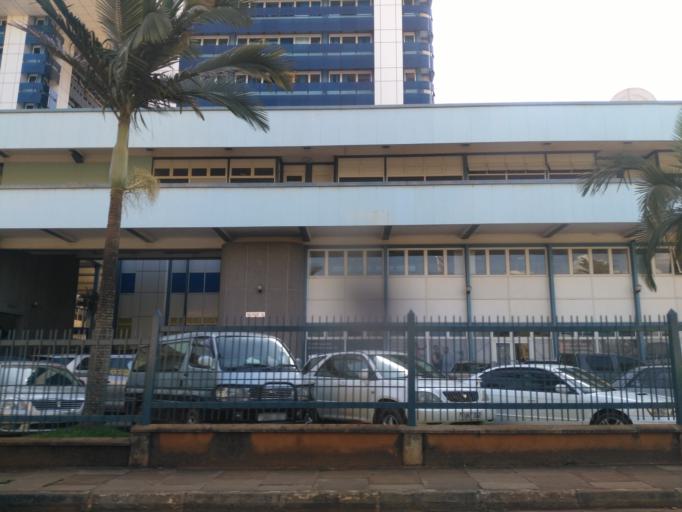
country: UG
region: Central Region
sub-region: Kampala District
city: Kampala
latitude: 0.3184
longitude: 32.5890
